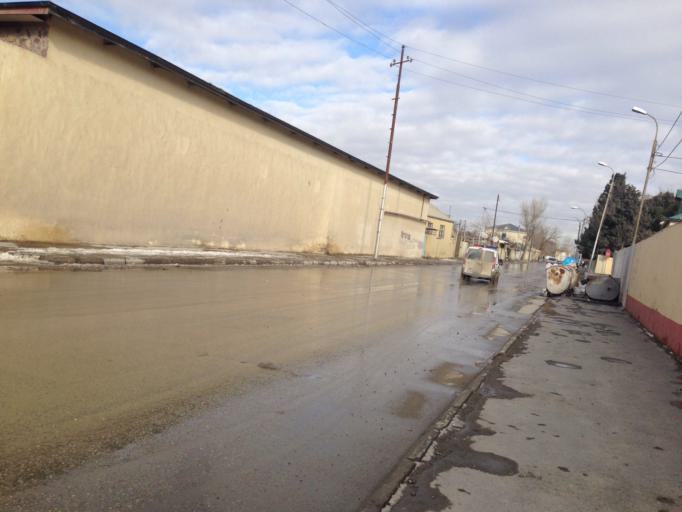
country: AZ
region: Baki
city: Baku
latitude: 40.3947
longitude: 49.8891
